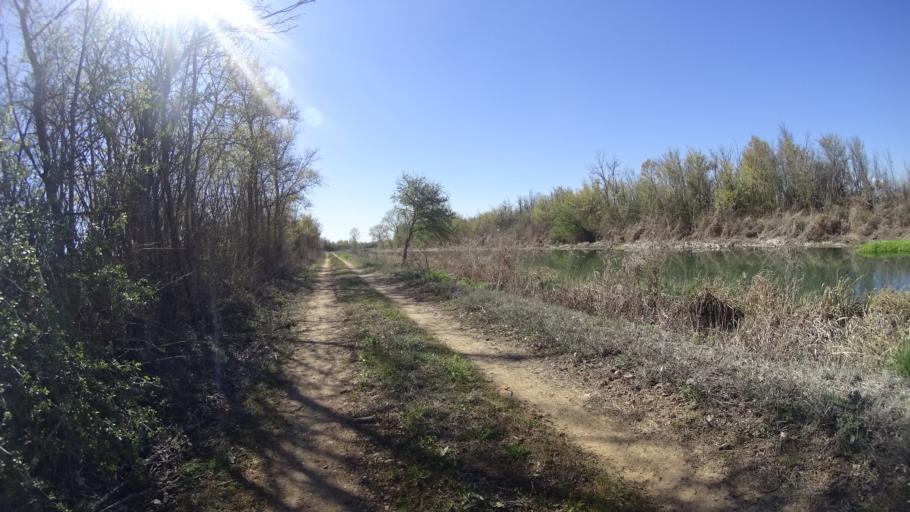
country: ES
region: Castille and Leon
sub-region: Provincia de Palencia
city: Osornillo
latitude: 42.4019
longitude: -4.3260
